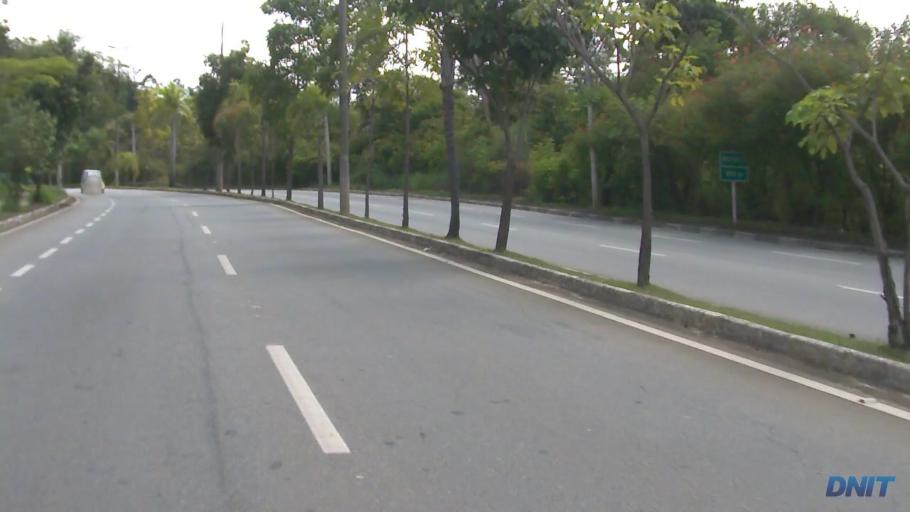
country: BR
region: Minas Gerais
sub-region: Coronel Fabriciano
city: Coronel Fabriciano
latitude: -19.5076
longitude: -42.5853
